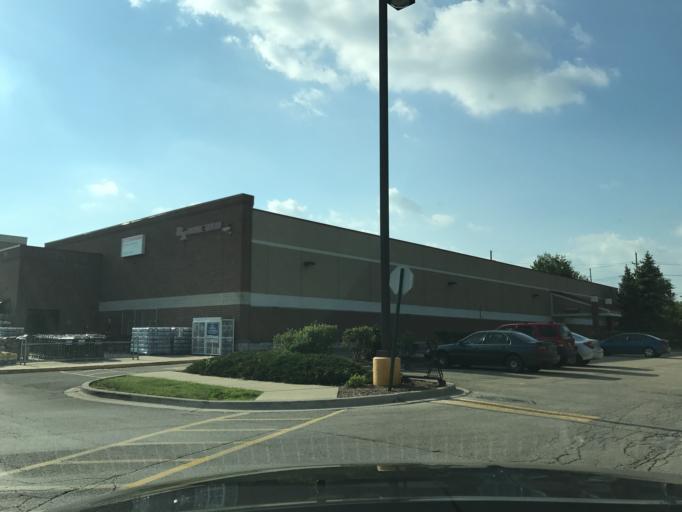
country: US
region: Illinois
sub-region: DuPage County
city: Naperville
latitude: 41.7865
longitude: -88.1443
